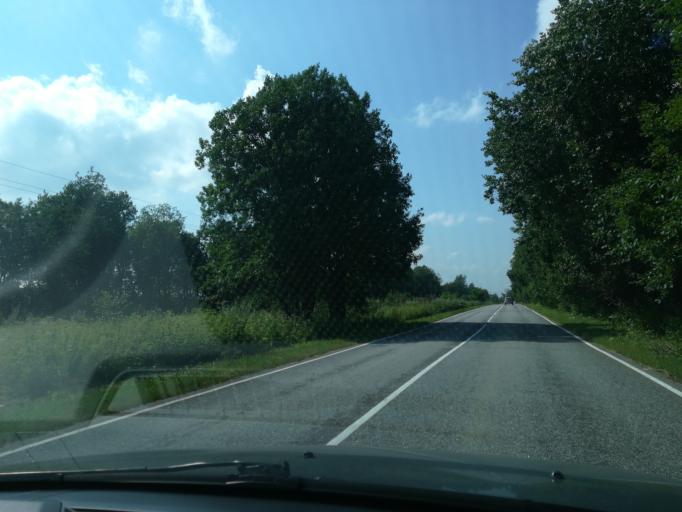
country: RU
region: Leningrad
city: Kopor'ye
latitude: 59.7286
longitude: 29.1132
